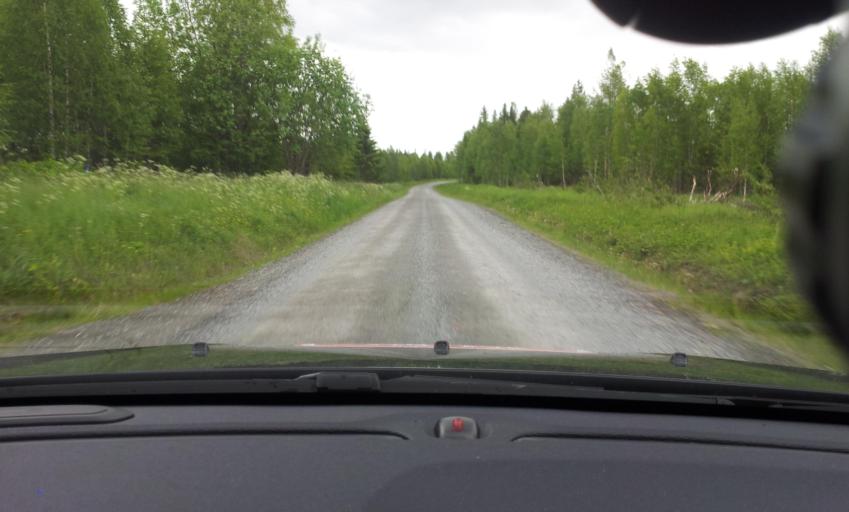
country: SE
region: Jaemtland
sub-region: OEstersunds Kommun
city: Brunflo
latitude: 63.1490
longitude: 15.0296
